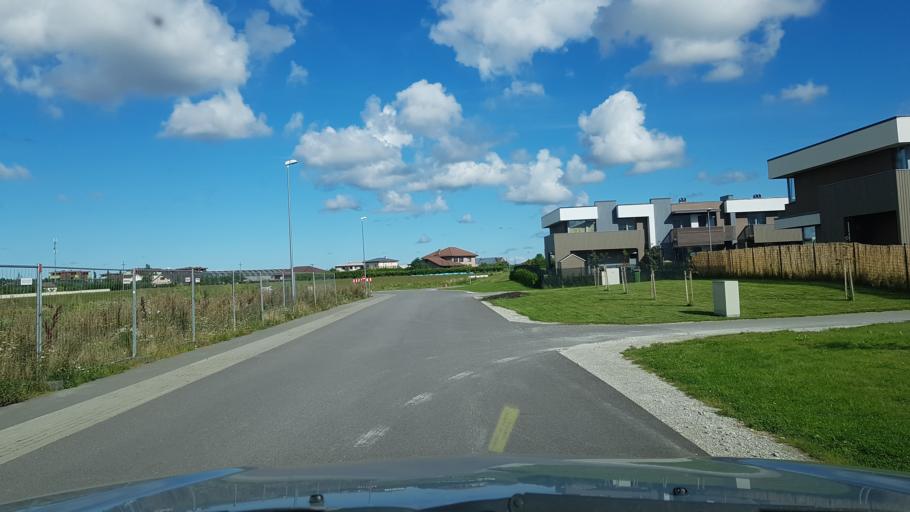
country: EE
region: Harju
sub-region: Tallinna linn
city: Tallinn
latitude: 59.3859
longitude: 24.8031
